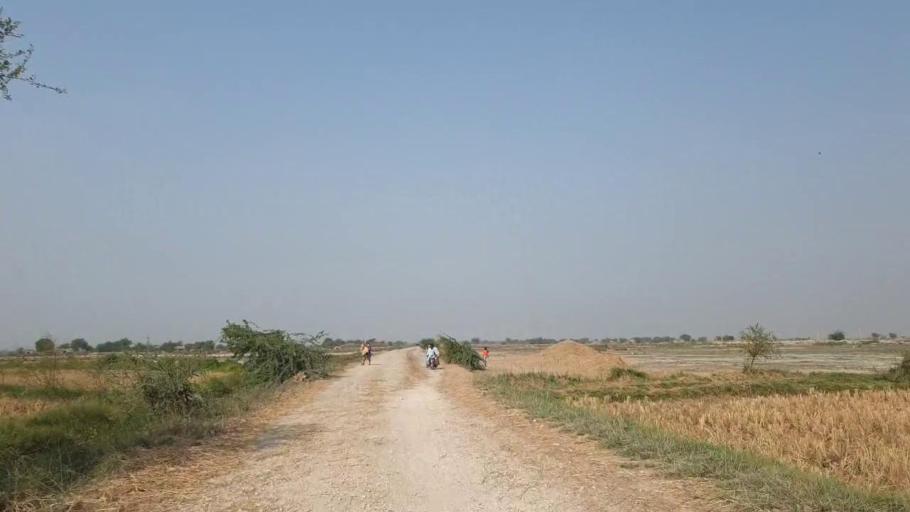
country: PK
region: Sindh
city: Kario
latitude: 24.9347
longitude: 68.5579
